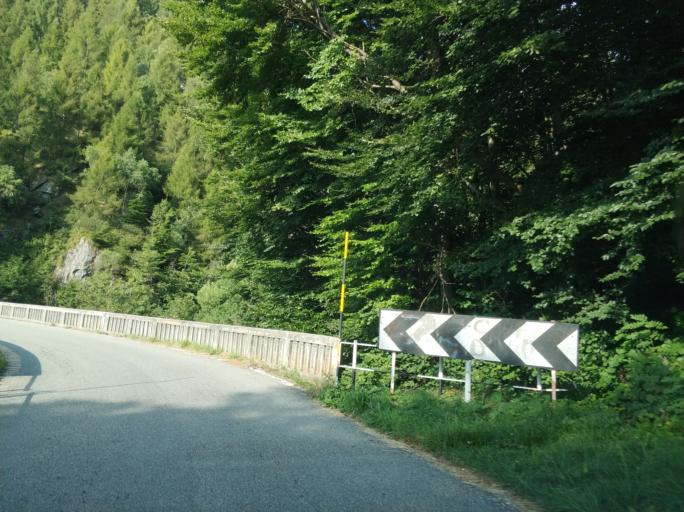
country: IT
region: Piedmont
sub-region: Provincia di Torino
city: Viu
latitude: 45.1909
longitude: 7.3638
